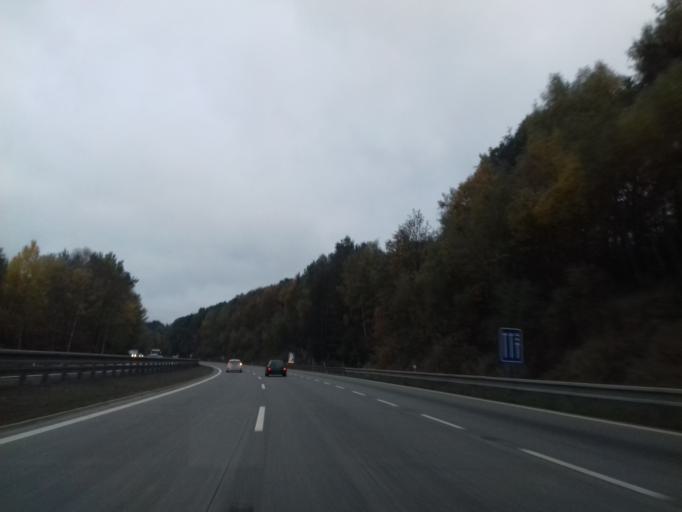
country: CZ
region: Central Bohemia
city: Vlasim
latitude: 49.7633
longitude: 14.9517
